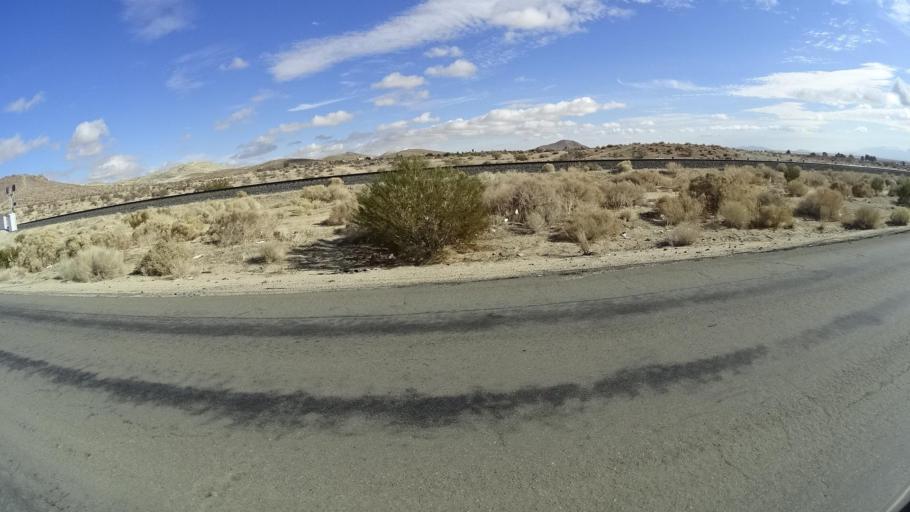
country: US
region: California
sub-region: Kern County
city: Rosamond
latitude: 34.8752
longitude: -118.1650
